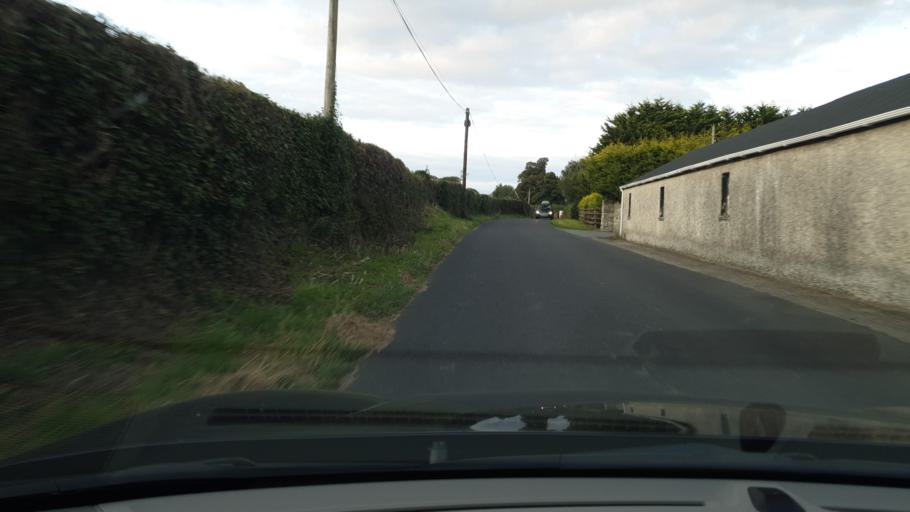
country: IE
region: Leinster
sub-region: South Dublin
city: Newcastle
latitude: 53.2580
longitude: -6.5283
